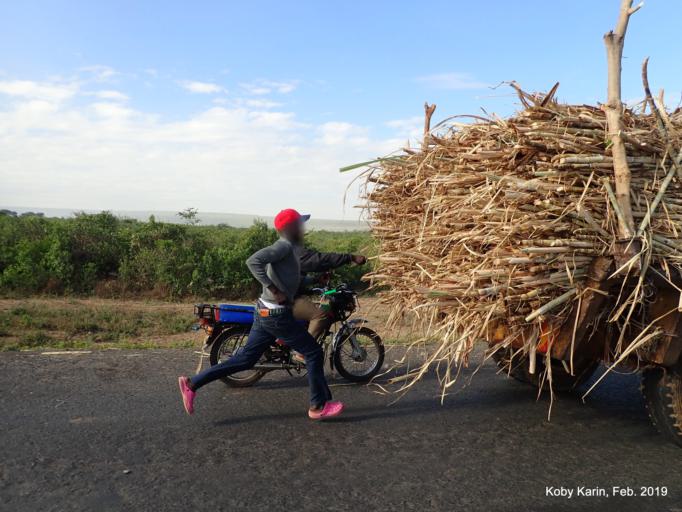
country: KE
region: Kisumu
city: Muhoroni
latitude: -0.1853
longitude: 35.1168
